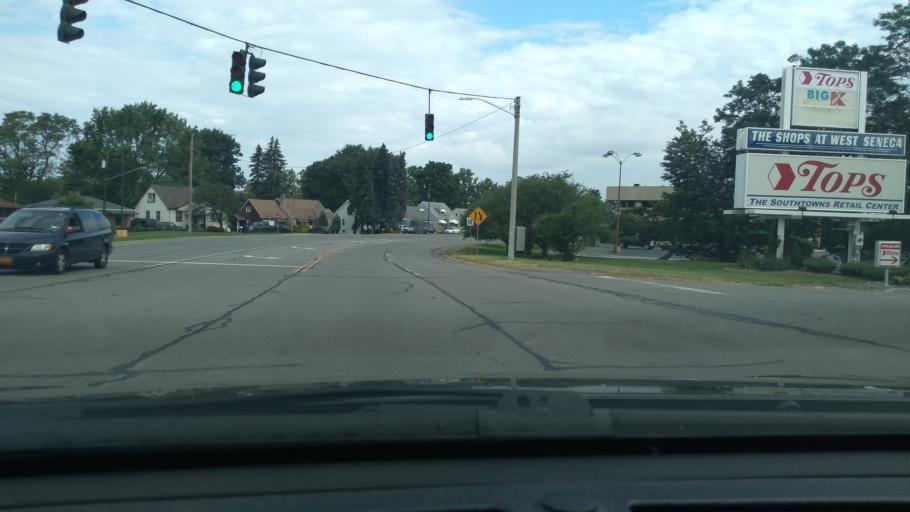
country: US
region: New York
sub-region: Erie County
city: West Seneca
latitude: 42.8302
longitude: -78.7884
